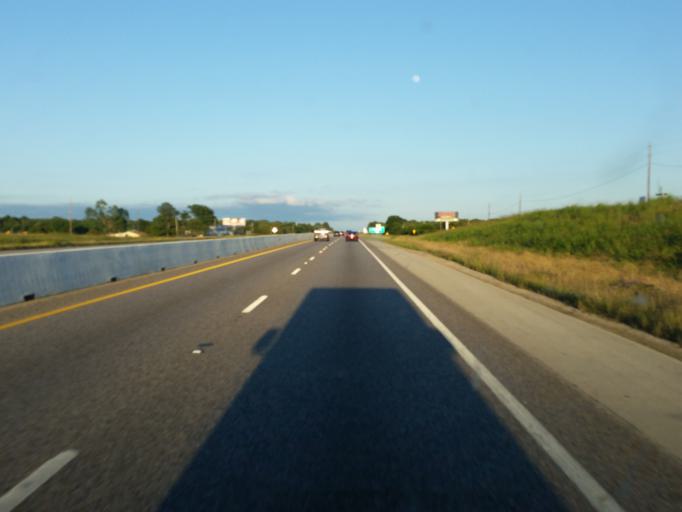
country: US
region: Texas
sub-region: Van Zandt County
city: Wills Point
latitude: 32.6153
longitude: -95.9716
